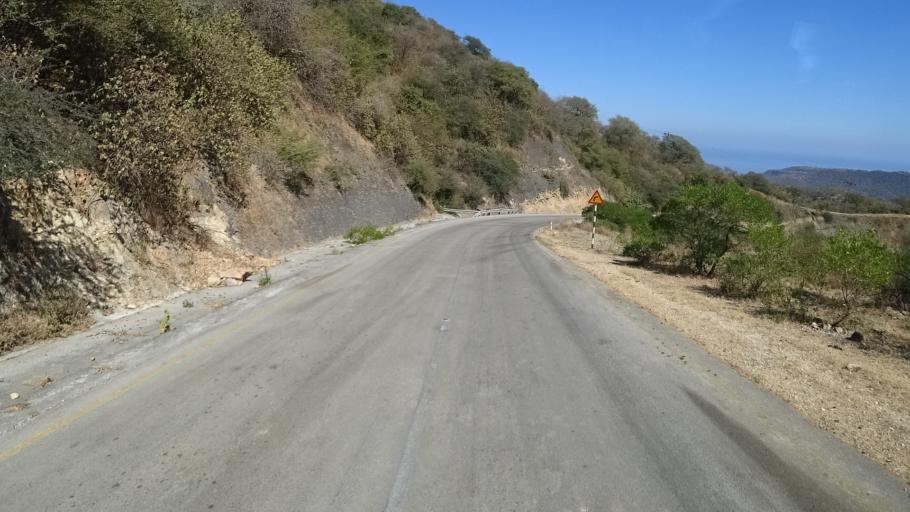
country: YE
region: Al Mahrah
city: Hawf
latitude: 16.7628
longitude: 53.3375
